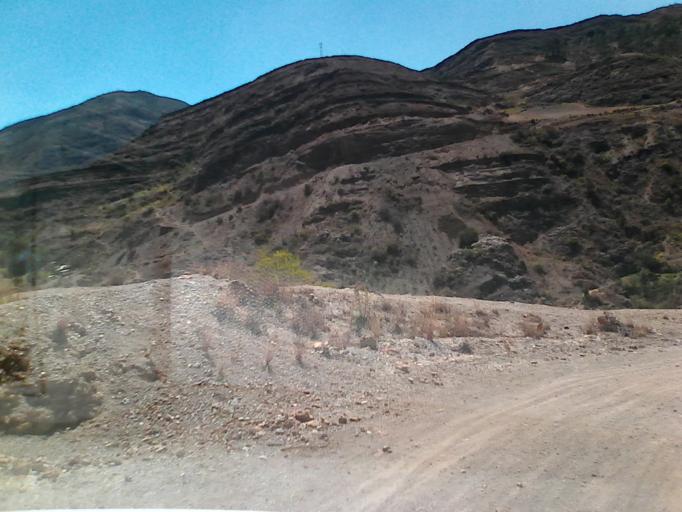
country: CO
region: Boyaca
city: Sachica
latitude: 5.5456
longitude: -73.5366
